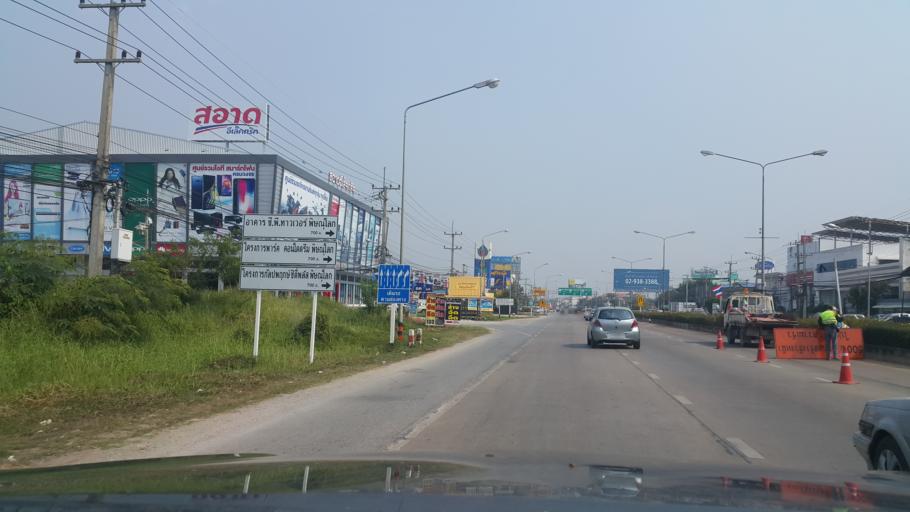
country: TH
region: Phitsanulok
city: Phitsanulok
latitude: 16.8186
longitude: 100.2878
